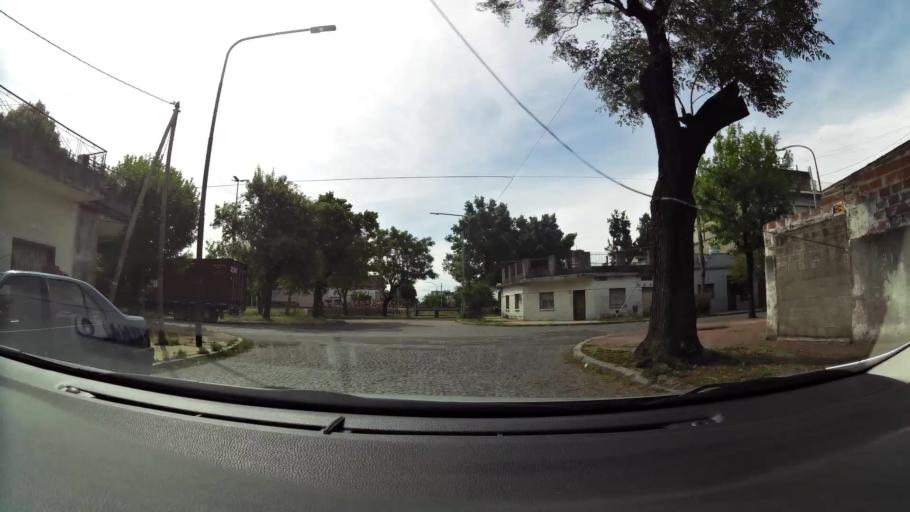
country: AR
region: Buenos Aires F.D.
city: Villa Lugano
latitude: -34.6583
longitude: -58.4321
